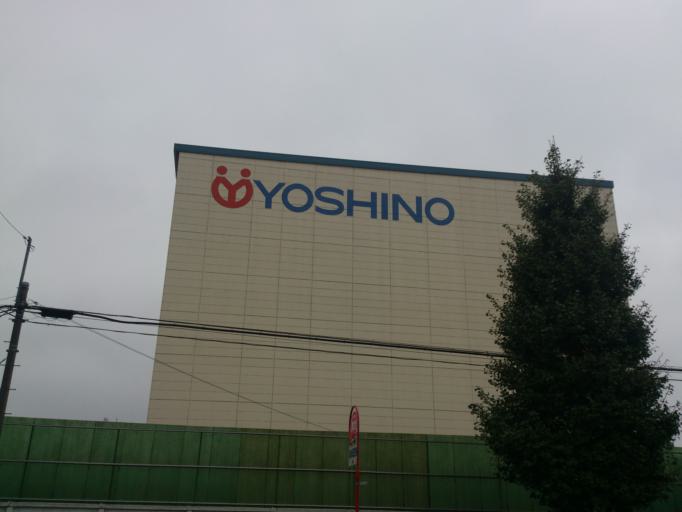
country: JP
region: Chiba
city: Matsudo
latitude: 35.7867
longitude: 139.9250
